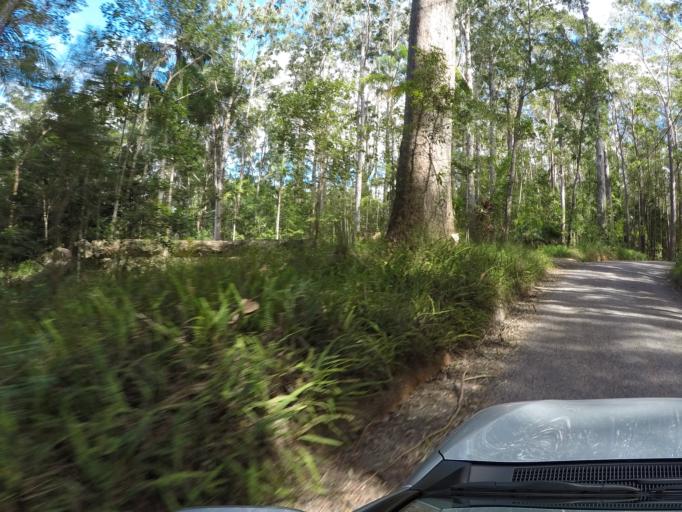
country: AU
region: Queensland
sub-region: Sunshine Coast
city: Nambour
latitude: -26.6183
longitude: 152.8564
